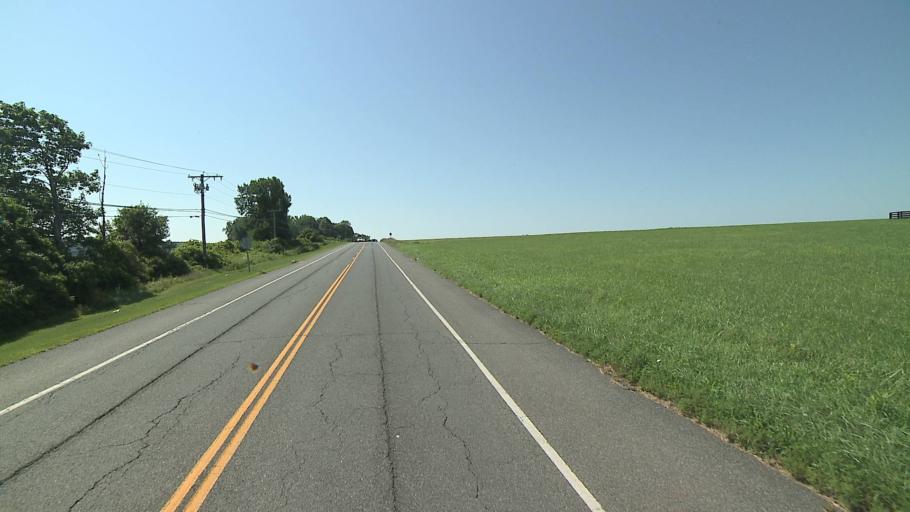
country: US
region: Connecticut
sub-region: Litchfield County
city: Canaan
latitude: 41.9300
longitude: -73.4439
